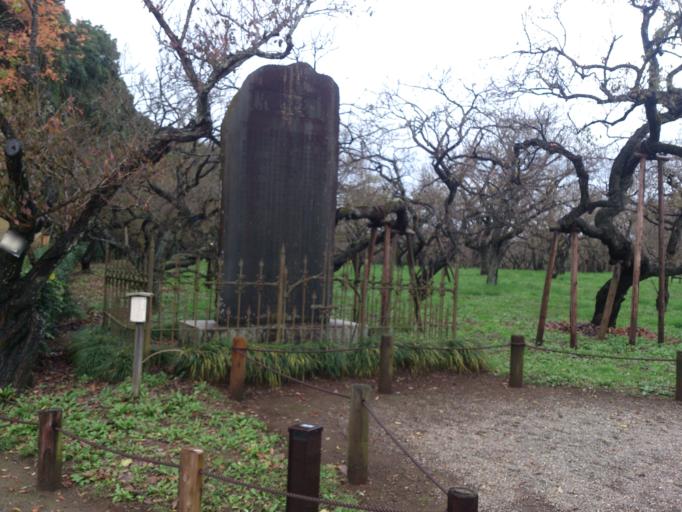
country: JP
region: Ibaraki
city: Mito-shi
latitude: 36.3745
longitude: 140.4537
